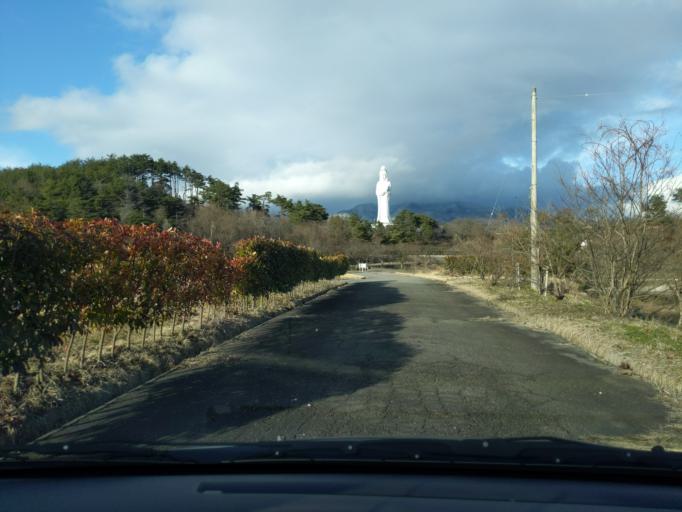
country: JP
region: Fukushima
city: Kitakata
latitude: 37.5499
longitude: 139.9508
